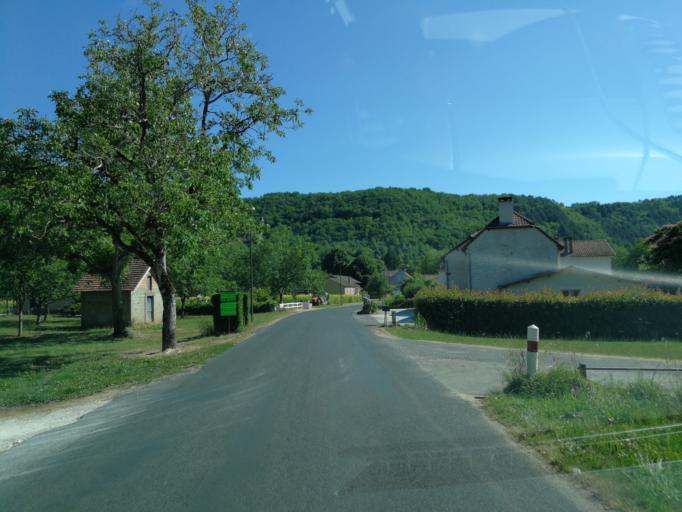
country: FR
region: Midi-Pyrenees
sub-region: Departement du Lot
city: Souillac
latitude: 44.8700
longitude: 1.4419
